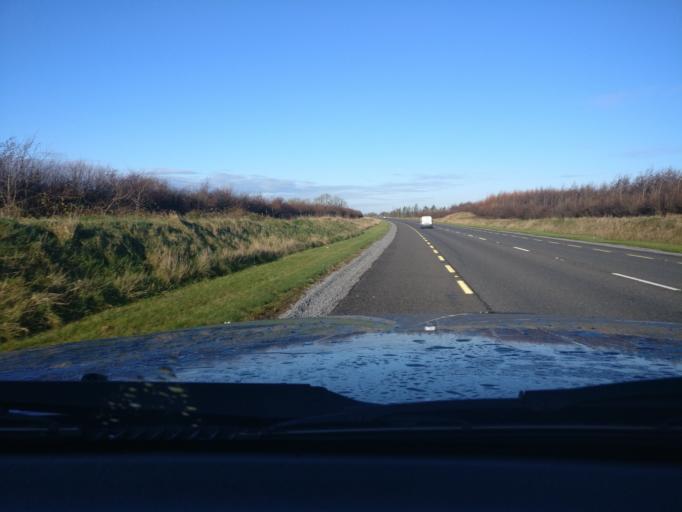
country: IE
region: Connaught
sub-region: County Galway
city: Loughrea
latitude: 53.2143
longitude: -8.5735
